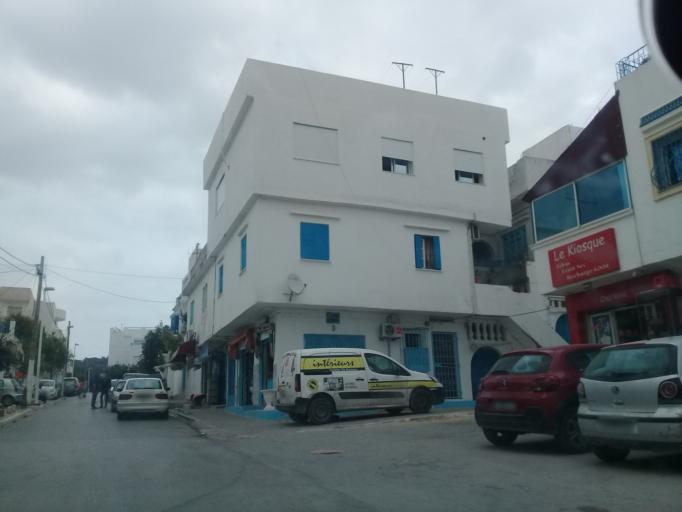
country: TN
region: Tunis
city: Sidi Bou Said
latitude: 36.8685
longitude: 10.3390
